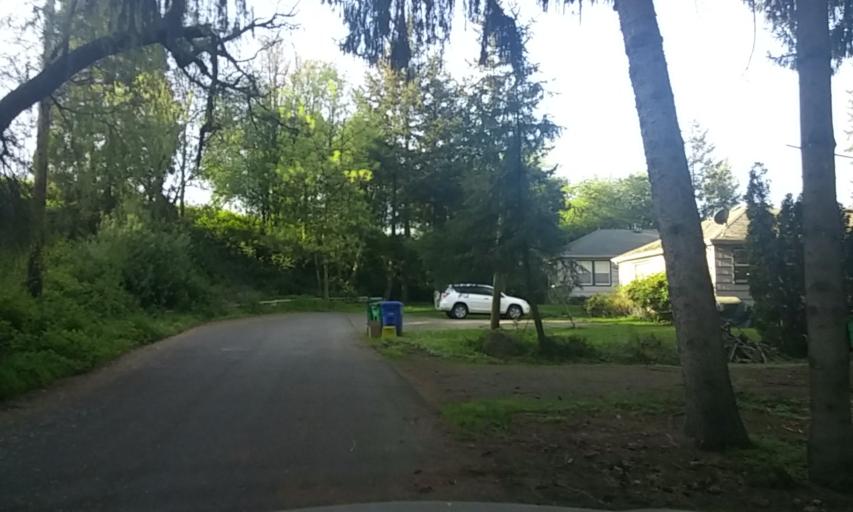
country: US
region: Oregon
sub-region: Washington County
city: Metzger
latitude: 45.4450
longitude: -122.7396
